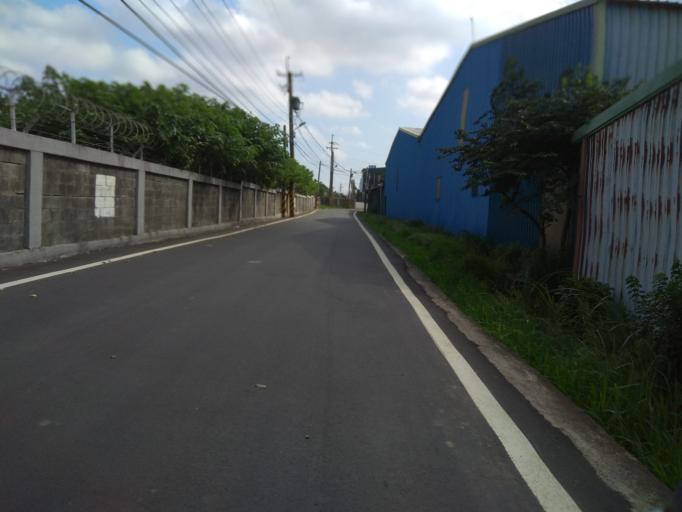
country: TW
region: Taiwan
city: Taoyuan City
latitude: 25.0578
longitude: 121.2169
